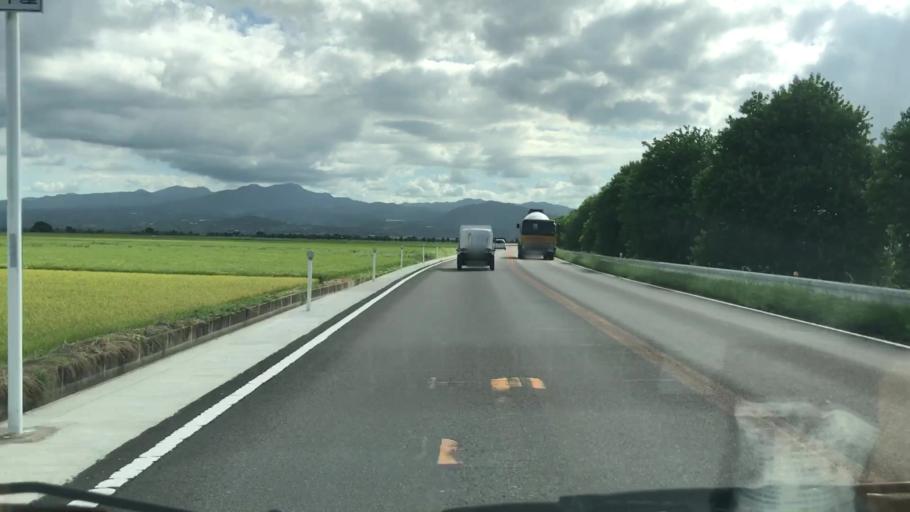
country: JP
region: Saga Prefecture
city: Kashima
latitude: 33.1406
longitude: 130.1442
